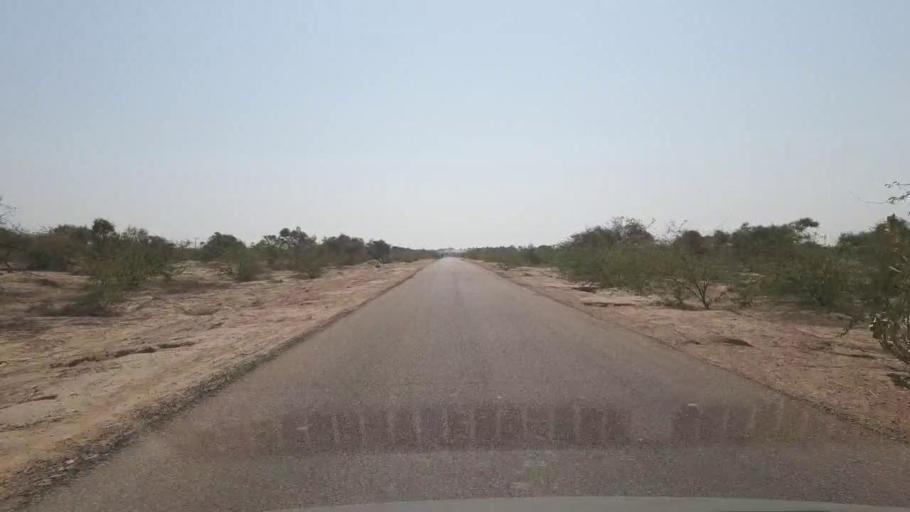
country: PK
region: Sindh
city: Chor
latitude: 25.5930
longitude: 70.1830
